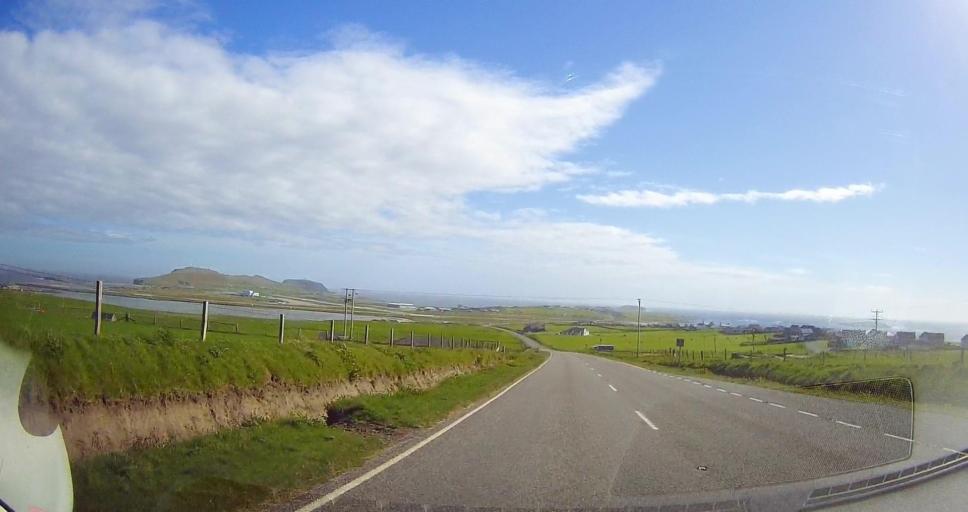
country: GB
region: Scotland
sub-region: Shetland Islands
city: Sandwick
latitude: 59.8928
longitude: -1.3031
